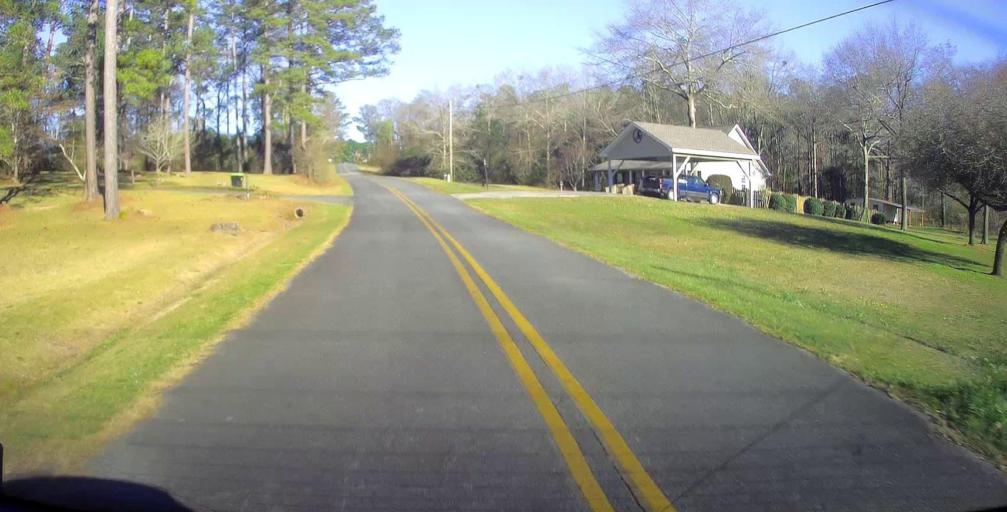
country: US
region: Georgia
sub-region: Taylor County
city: Reynolds
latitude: 32.5513
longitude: -84.0970
